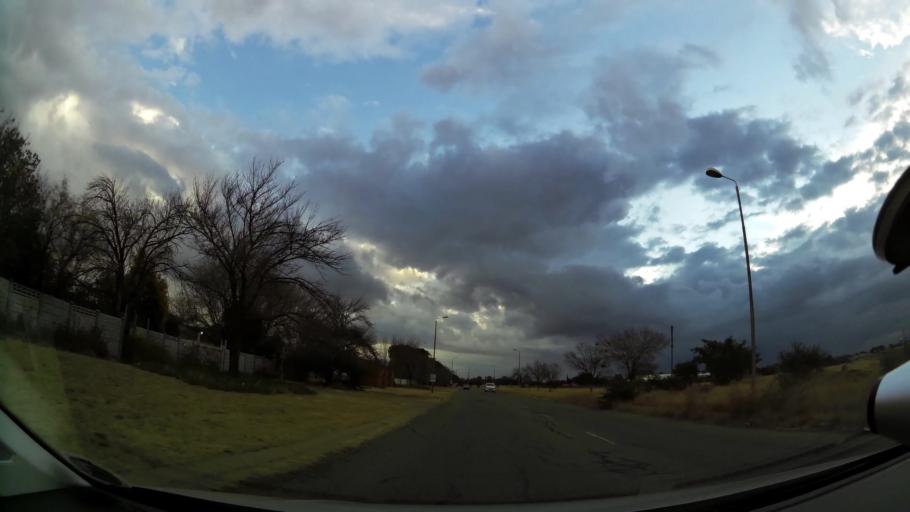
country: ZA
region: Orange Free State
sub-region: Lejweleputswa District Municipality
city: Welkom
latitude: -27.9544
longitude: 26.7388
